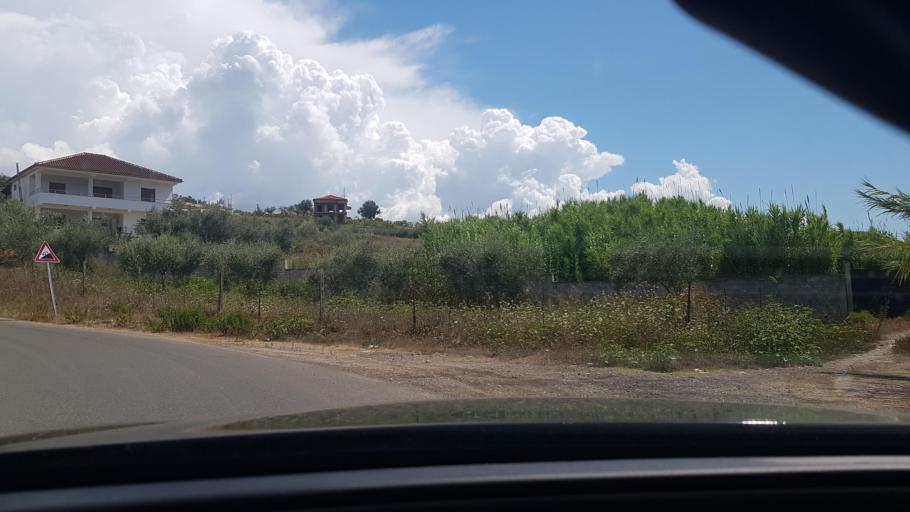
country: AL
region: Durres
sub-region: Rrethi i Durresit
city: Rrashbull
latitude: 41.2976
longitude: 19.5247
